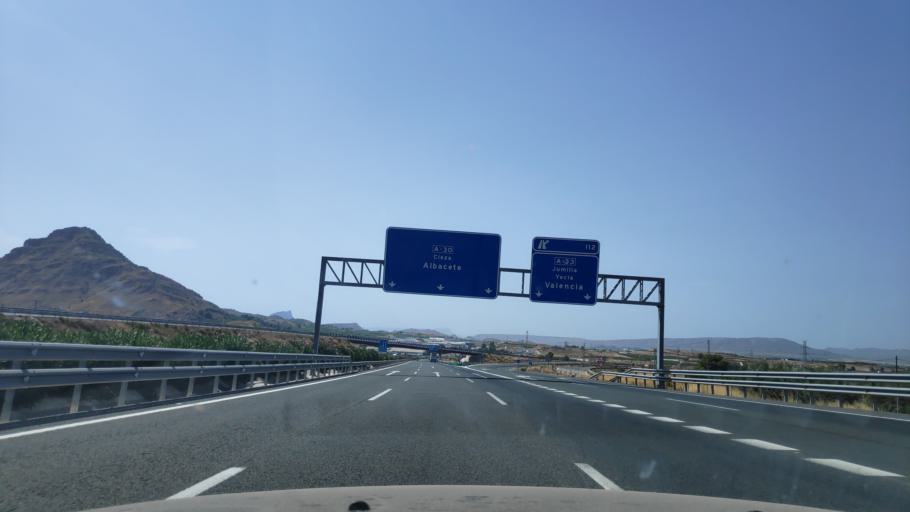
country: ES
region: Murcia
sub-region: Murcia
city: Ojos
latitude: 38.1845
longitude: -1.3208
